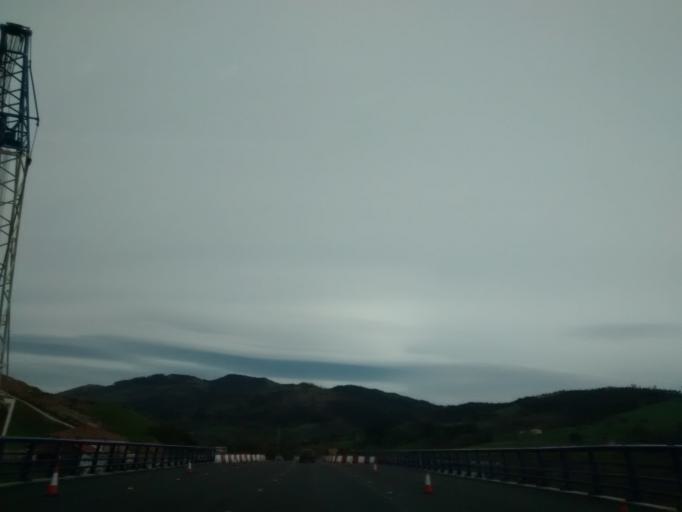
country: ES
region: Cantabria
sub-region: Provincia de Cantabria
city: Puente Viesgo
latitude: 43.3137
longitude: -3.9472
